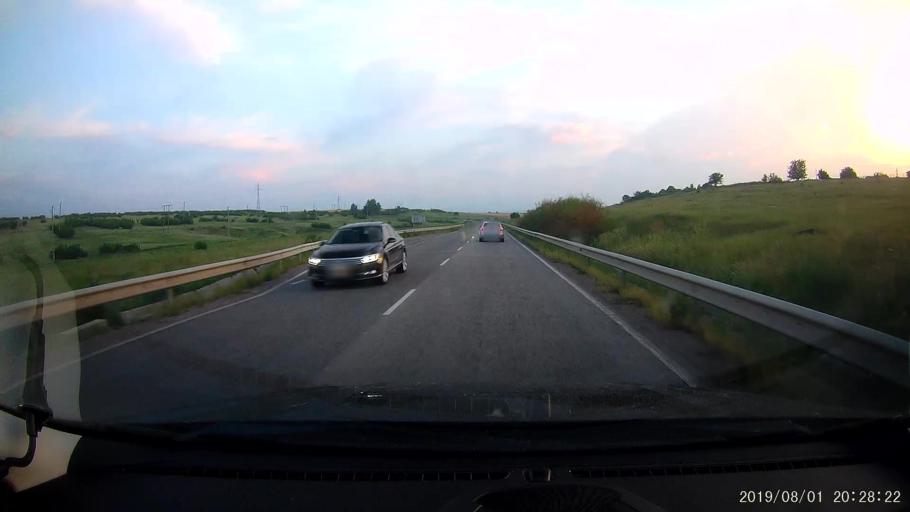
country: BG
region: Yambol
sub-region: Obshtina Elkhovo
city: Elkhovo
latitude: 42.1695
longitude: 26.5788
